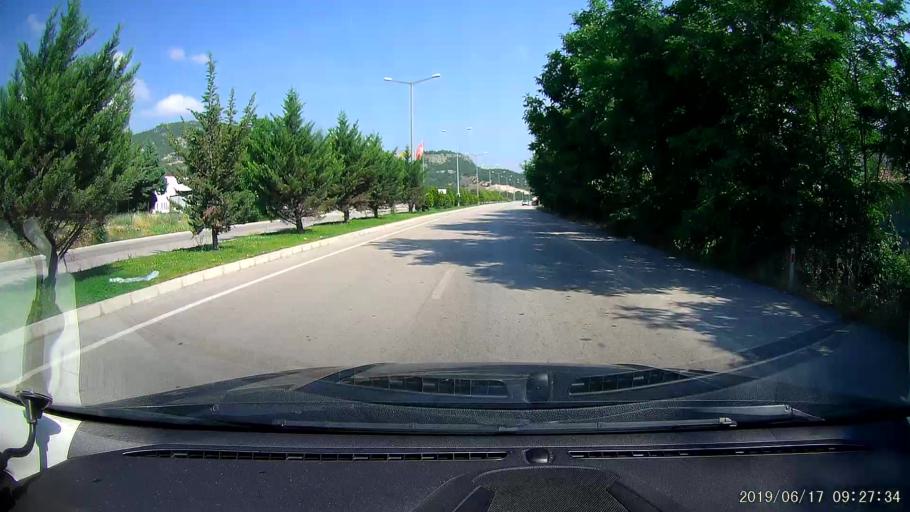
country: TR
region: Amasya
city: Amasya
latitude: 40.6784
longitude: 35.8256
